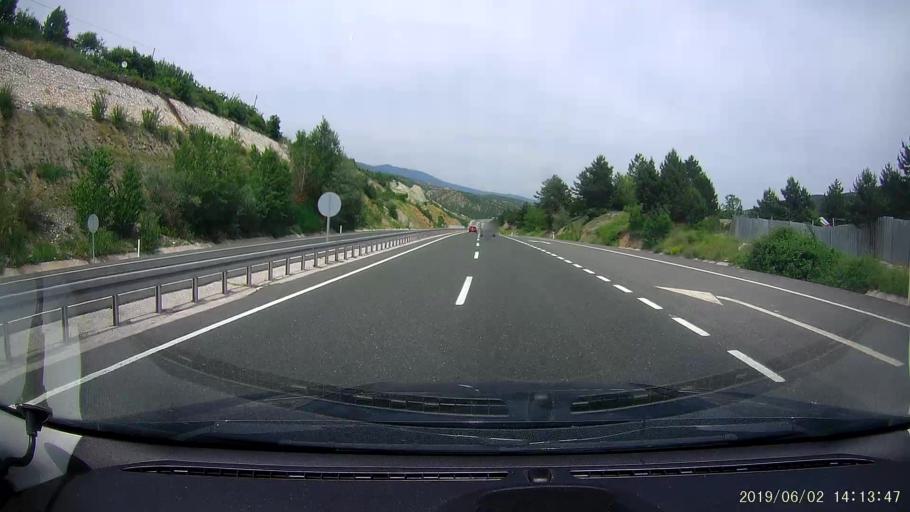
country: TR
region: Cankiri
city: Yaprakli
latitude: 40.9277
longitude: 33.8395
